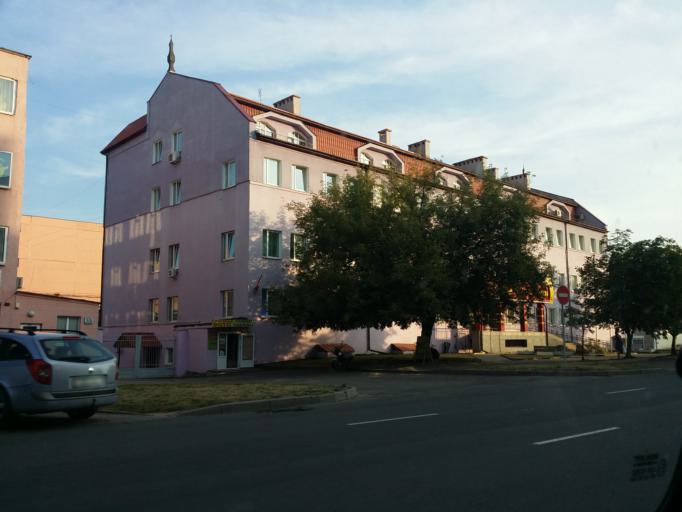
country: BY
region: Minsk
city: Minsk
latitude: 53.9129
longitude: 27.5995
